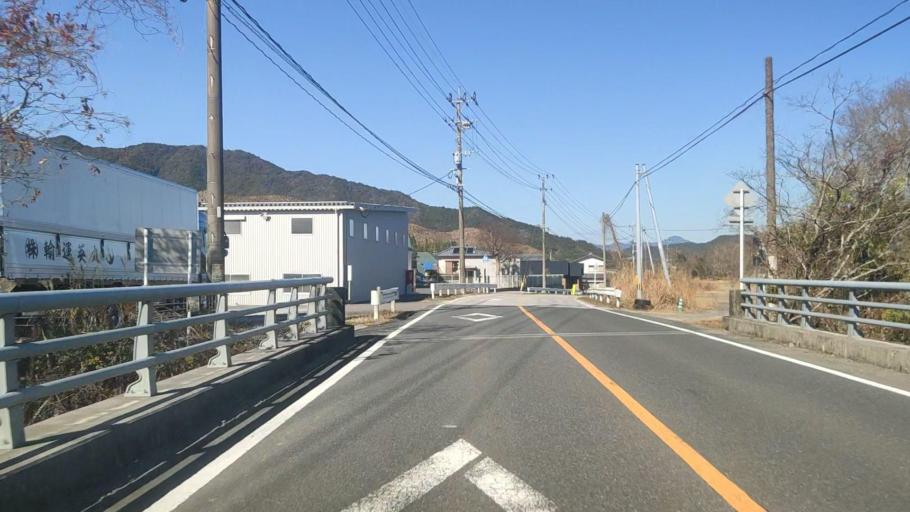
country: JP
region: Oita
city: Saiki
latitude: 32.9077
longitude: 131.9309
